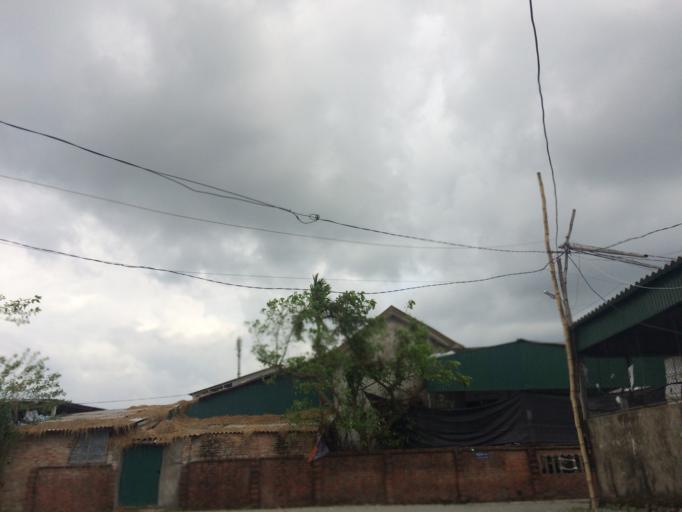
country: VN
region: Ha Tinh
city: Ha Tinh
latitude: 18.3332
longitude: 105.9212
